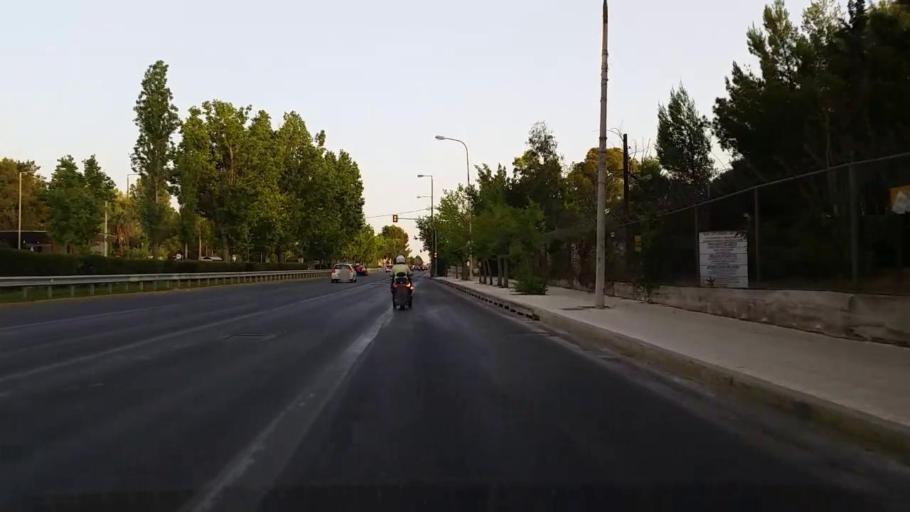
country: GR
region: Attica
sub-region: Nomarchia Athinas
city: Argyroupoli
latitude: 37.9039
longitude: 23.7456
